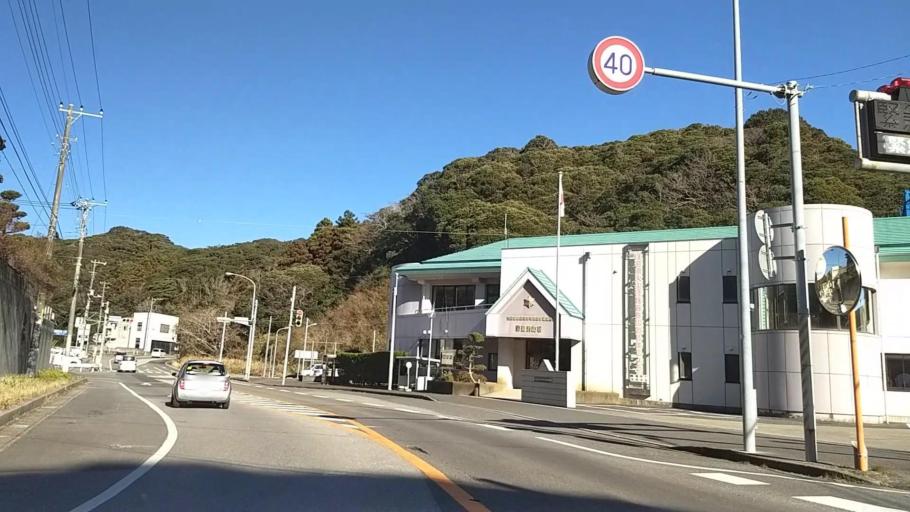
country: JP
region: Chiba
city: Katsuura
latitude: 35.1552
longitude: 140.3230
